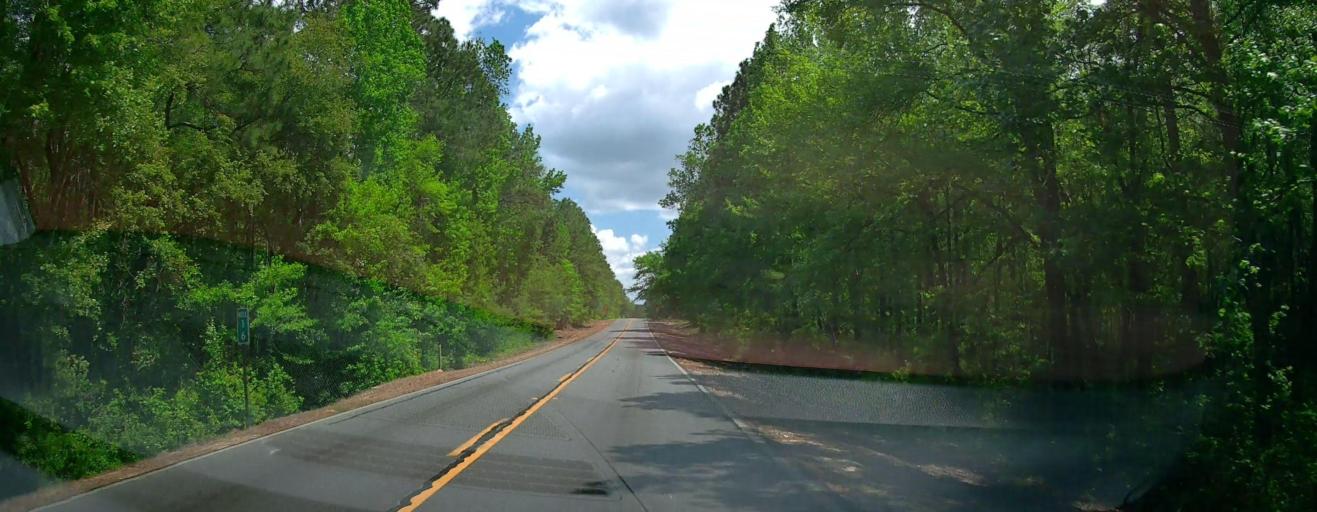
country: US
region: Georgia
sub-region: Treutlen County
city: Soperton
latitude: 32.5041
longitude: -82.6197
